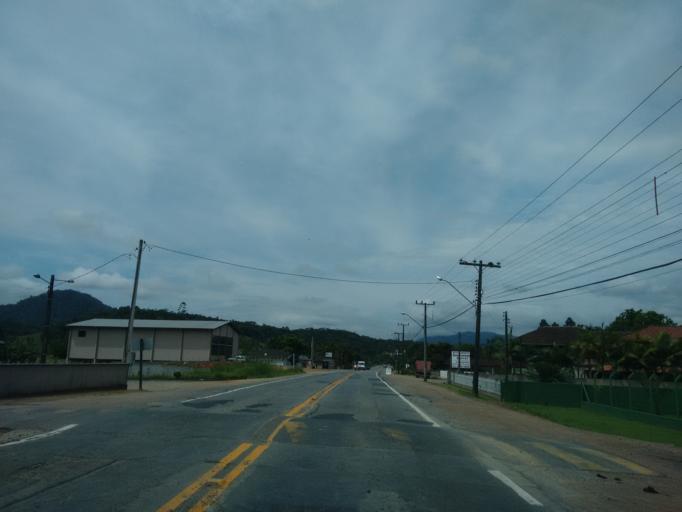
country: BR
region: Santa Catarina
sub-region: Pomerode
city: Pomerode
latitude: -26.6822
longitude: -49.1477
